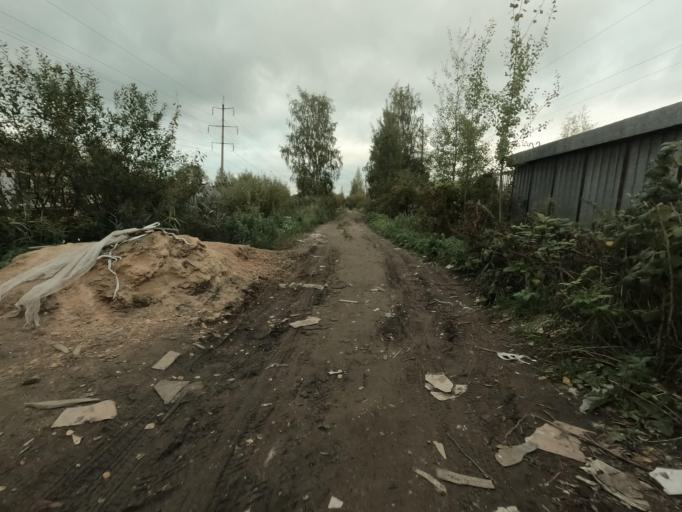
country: RU
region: St.-Petersburg
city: Sapernyy
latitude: 59.7770
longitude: 30.6431
